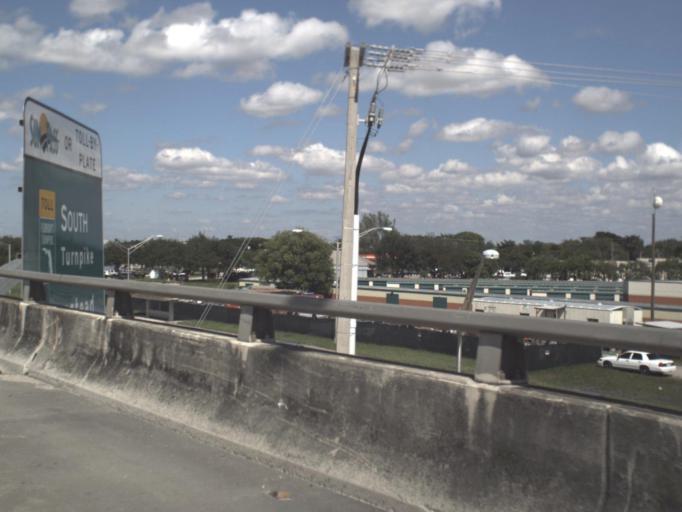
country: US
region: Florida
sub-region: Miami-Dade County
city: South Miami Heights
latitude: 25.5953
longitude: -80.3718
